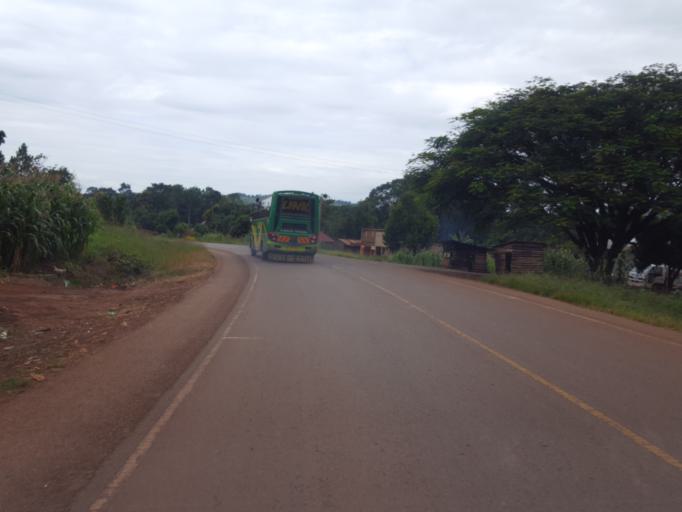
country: UG
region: Central Region
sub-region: Mityana District
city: Mityana
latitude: 0.6696
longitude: 32.0864
